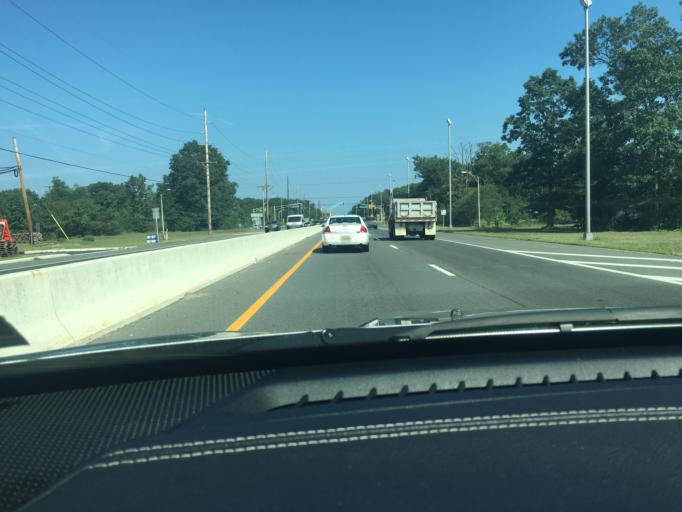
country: US
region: New Jersey
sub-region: Ocean County
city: Leisure Village
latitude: 40.0501
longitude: -74.1987
